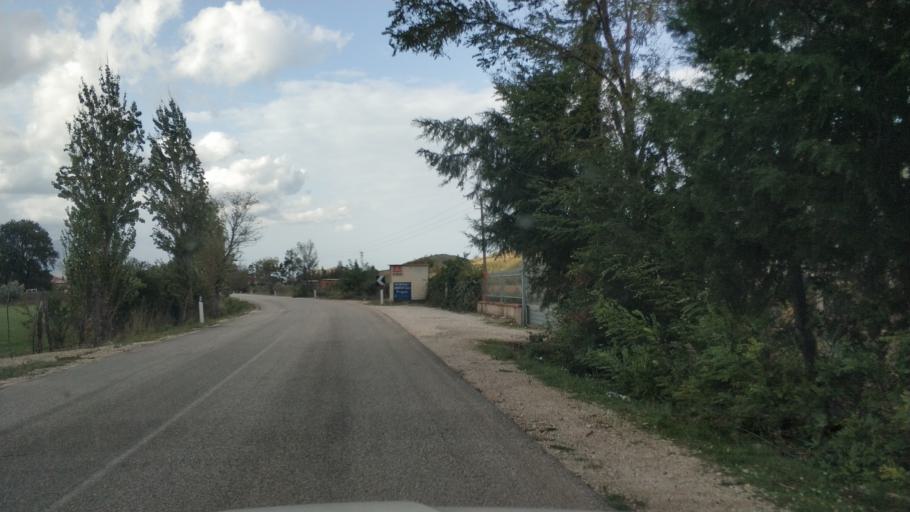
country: AL
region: Vlore
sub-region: Rrethi i Vlores
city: Orikum
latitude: 40.2801
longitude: 19.5026
